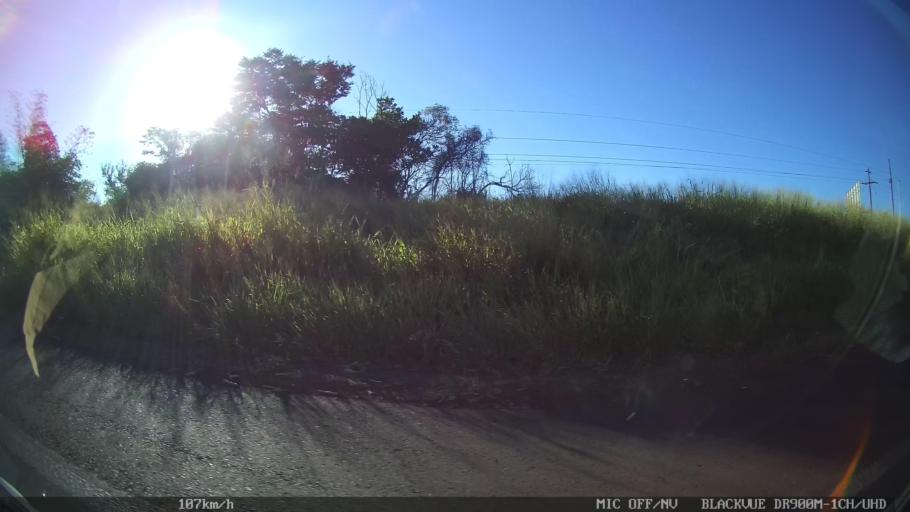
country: BR
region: Sao Paulo
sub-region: Olimpia
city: Olimpia
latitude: -20.7337
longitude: -49.0683
